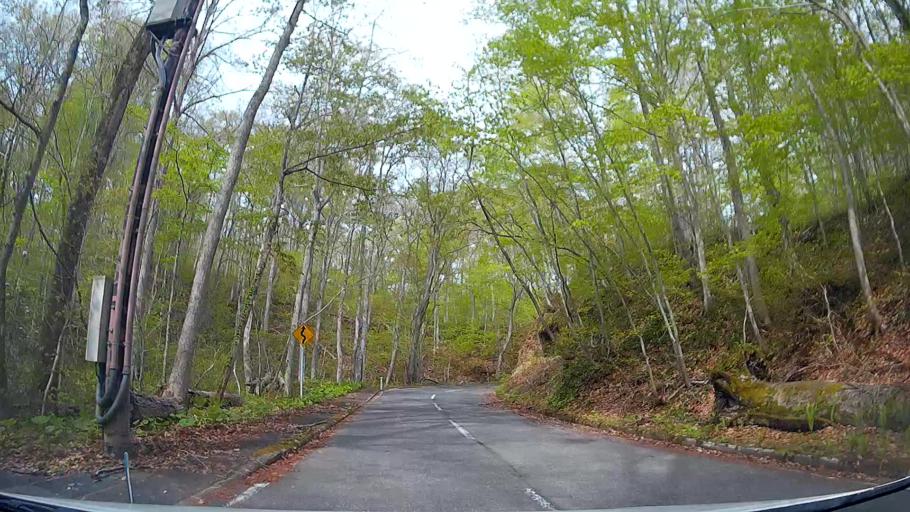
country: JP
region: Akita
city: Hanawa
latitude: 40.4283
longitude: 140.9129
